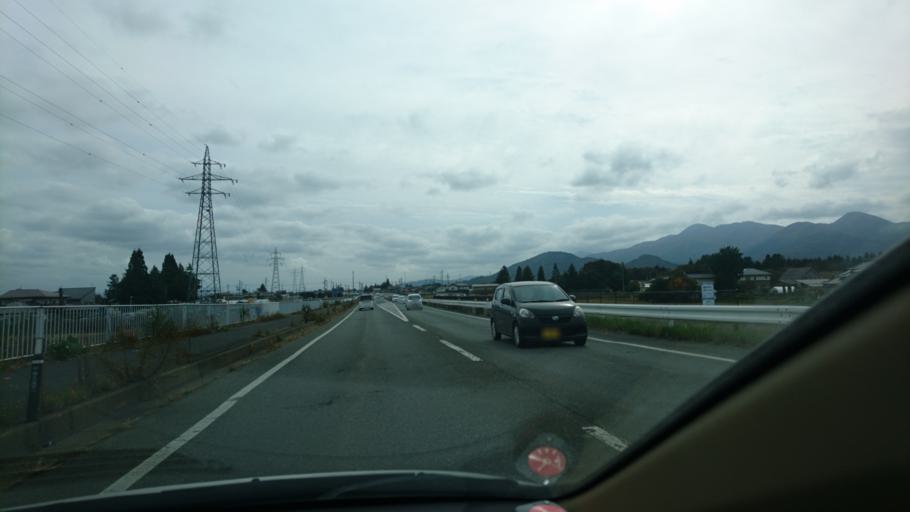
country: JP
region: Iwate
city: Morioka-shi
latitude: 39.7026
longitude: 141.1026
